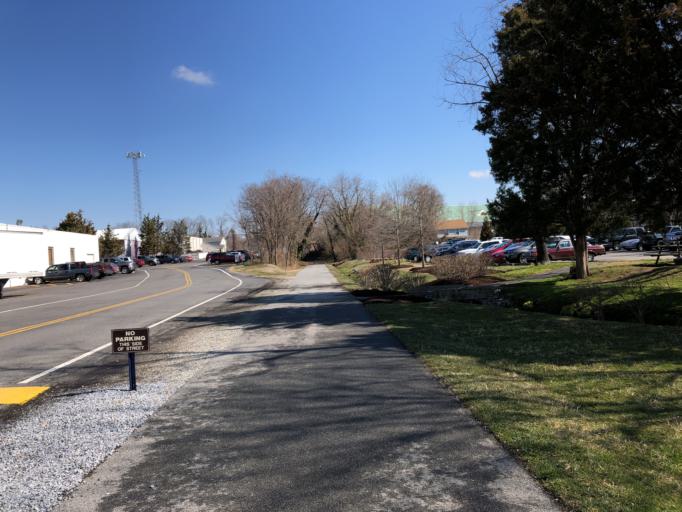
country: US
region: Maryland
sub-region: Kent County
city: Chestertown
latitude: 39.2147
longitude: -76.0730
